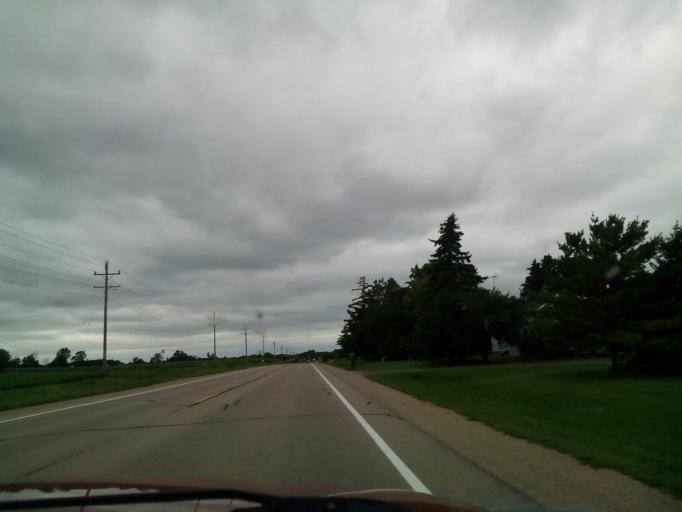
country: US
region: Wisconsin
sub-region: Waupaca County
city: Weyauwega
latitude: 44.2616
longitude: -88.8387
